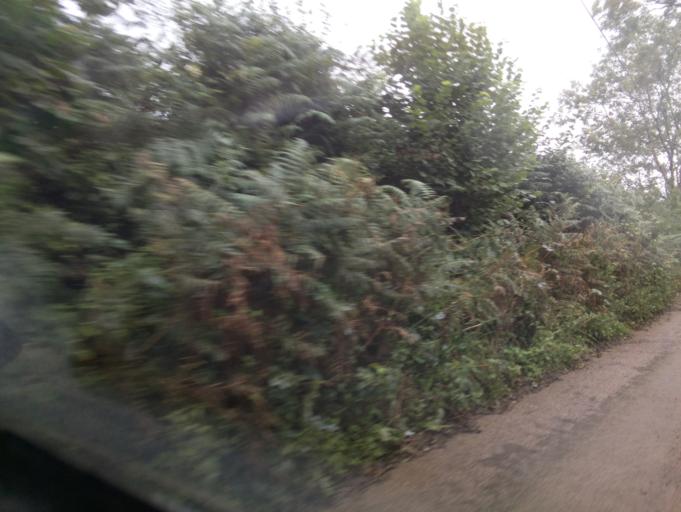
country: GB
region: England
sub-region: Devon
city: Totnes
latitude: 50.3405
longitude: -3.6847
